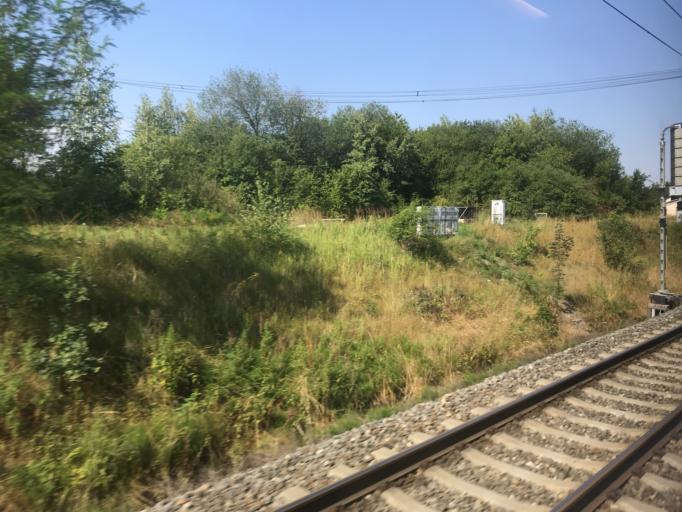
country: CZ
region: Central Bohemia
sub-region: Okres Praha-Vychod
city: Strancice
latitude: 49.9531
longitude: 14.6642
